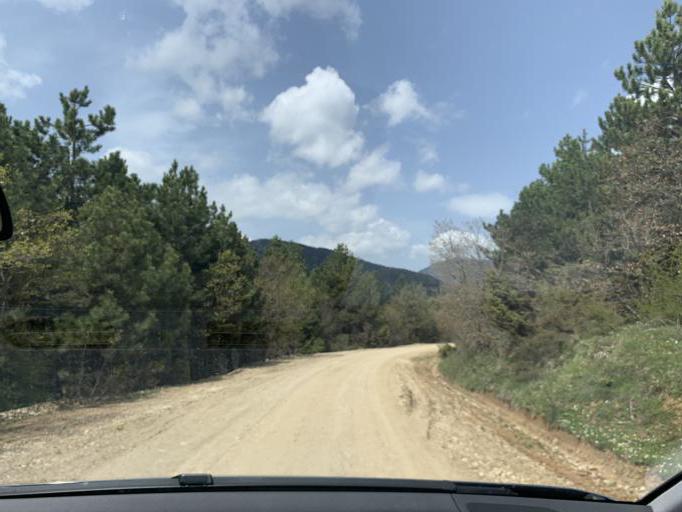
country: TR
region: Bolu
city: Bolu
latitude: 40.8306
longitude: 31.6747
